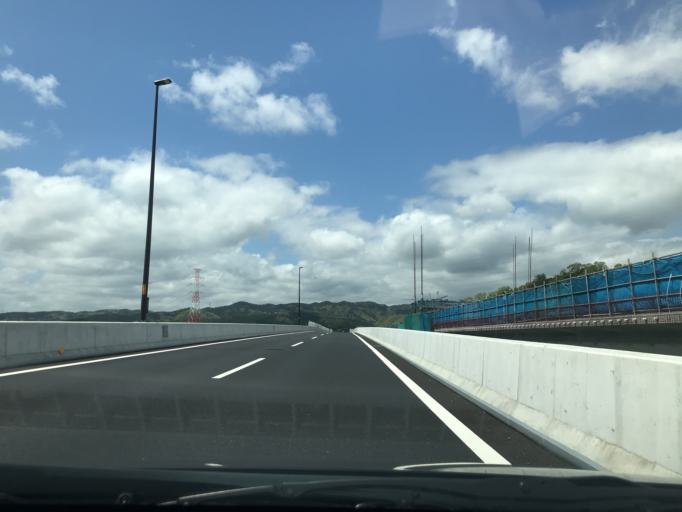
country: JP
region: Osaka
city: Takatsuki
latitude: 34.8852
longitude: 135.6177
